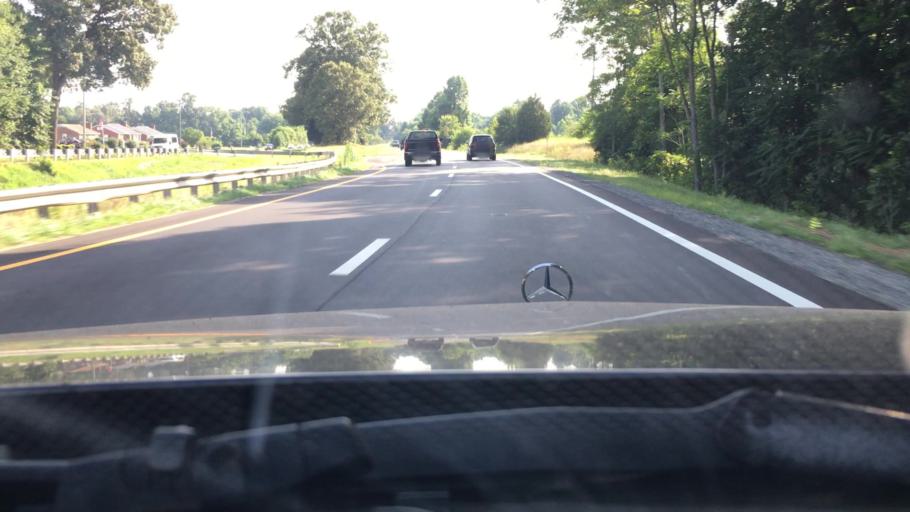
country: US
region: Virginia
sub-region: Amherst County
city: Amherst
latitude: 37.6369
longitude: -78.9916
